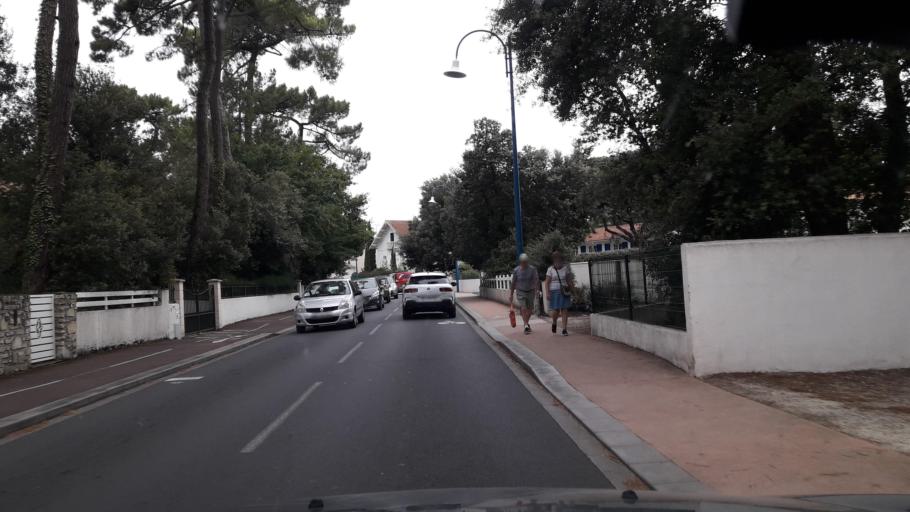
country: FR
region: Poitou-Charentes
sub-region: Departement de la Charente-Maritime
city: Les Mathes
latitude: 45.6929
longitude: -1.1788
